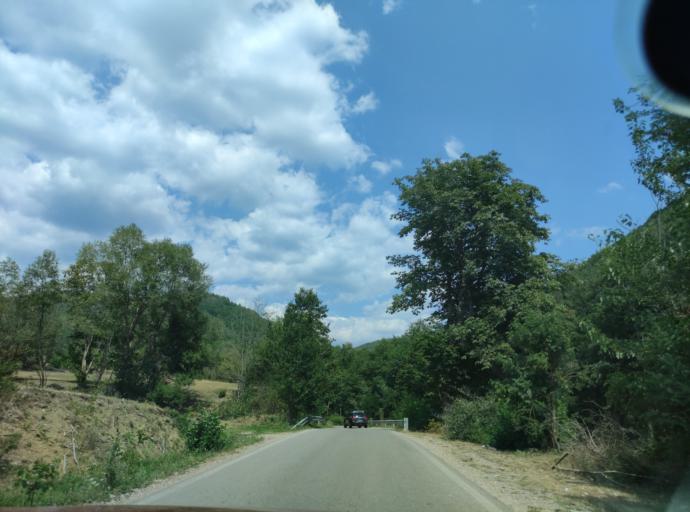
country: BG
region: Blagoevgrad
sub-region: Obshtina Belitsa
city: Belitsa
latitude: 41.9991
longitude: 23.5496
